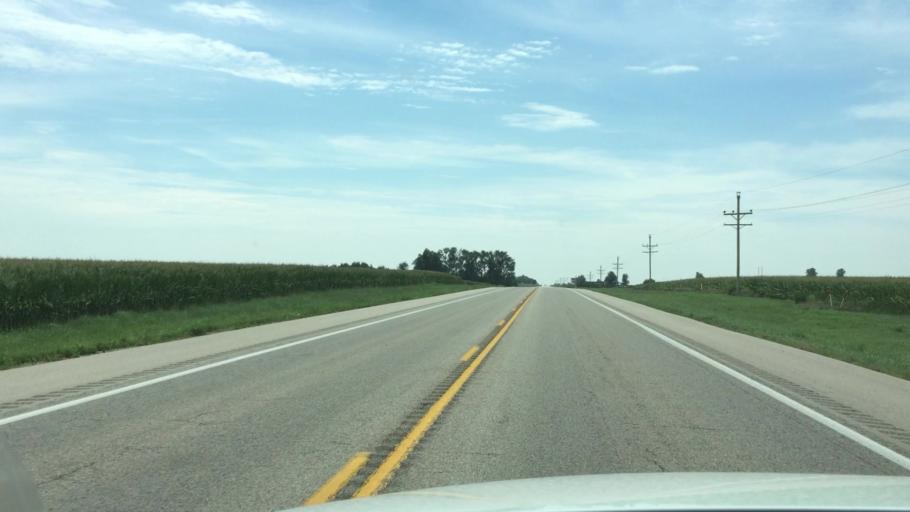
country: US
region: Kansas
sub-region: Nemaha County
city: Sabetha
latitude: 39.7662
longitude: -95.7296
